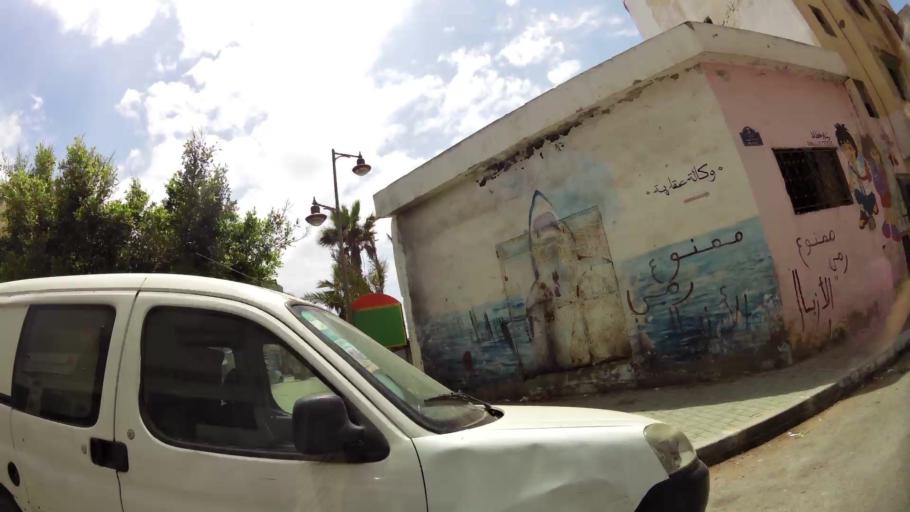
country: MA
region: Rabat-Sale-Zemmour-Zaer
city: Sale
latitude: 34.0514
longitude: -6.8220
